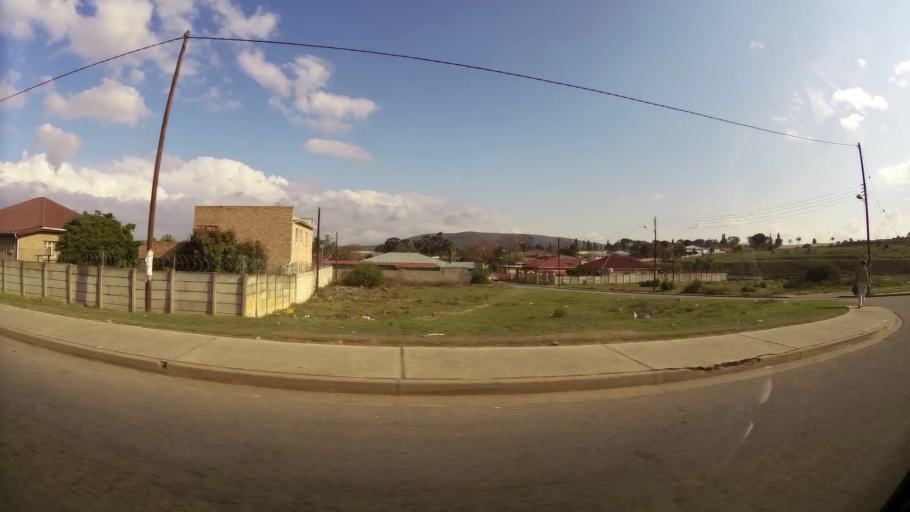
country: ZA
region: Eastern Cape
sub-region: Nelson Mandela Bay Metropolitan Municipality
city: Uitenhage
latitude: -33.7597
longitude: 25.3889
